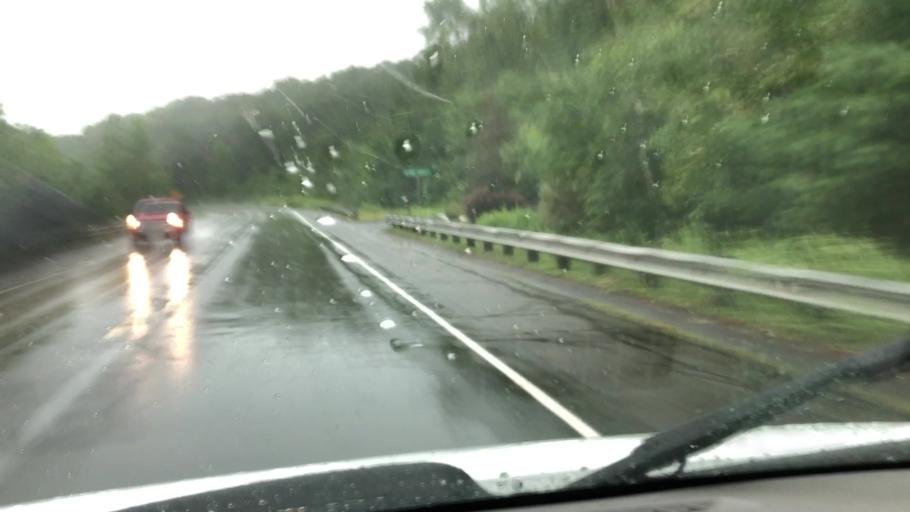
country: US
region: Massachusetts
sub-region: Berkshire County
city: Pittsfield
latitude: 42.4169
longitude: -73.2748
